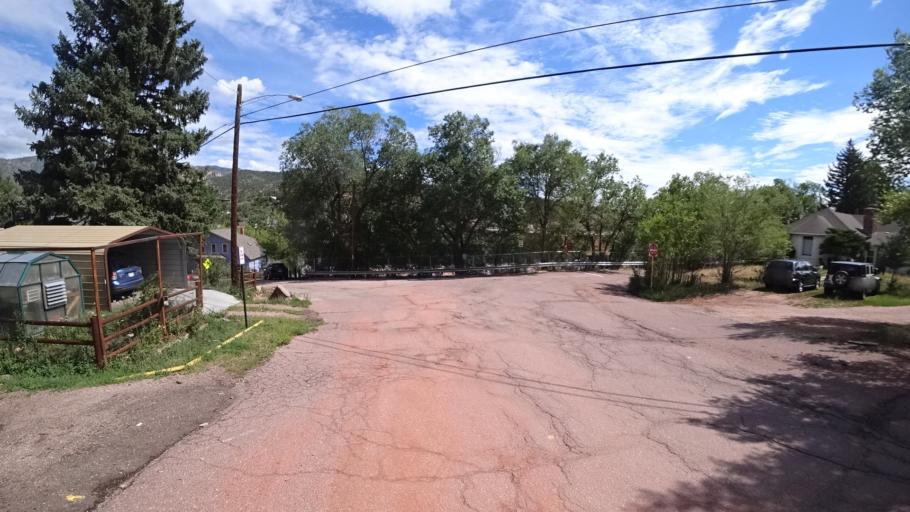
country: US
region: Colorado
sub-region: El Paso County
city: Manitou Springs
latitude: 38.8552
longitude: -104.9156
